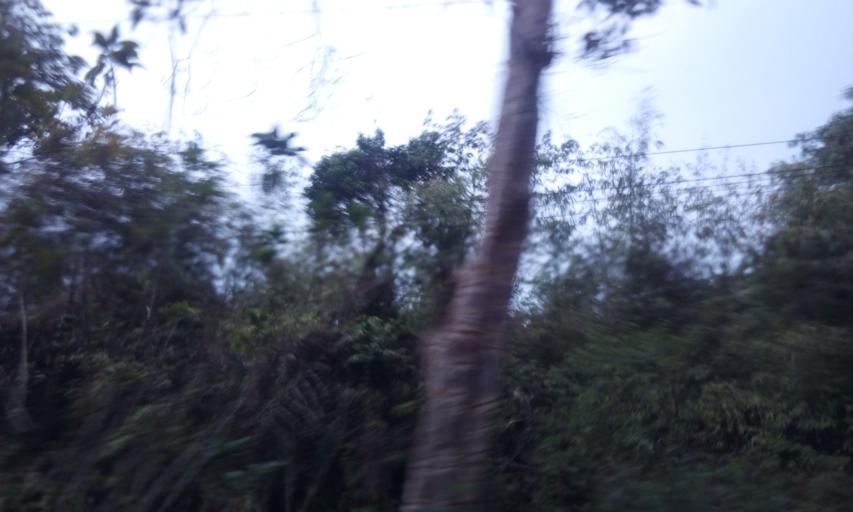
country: TH
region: Trat
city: Khao Saming
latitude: 12.3337
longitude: 102.3702
